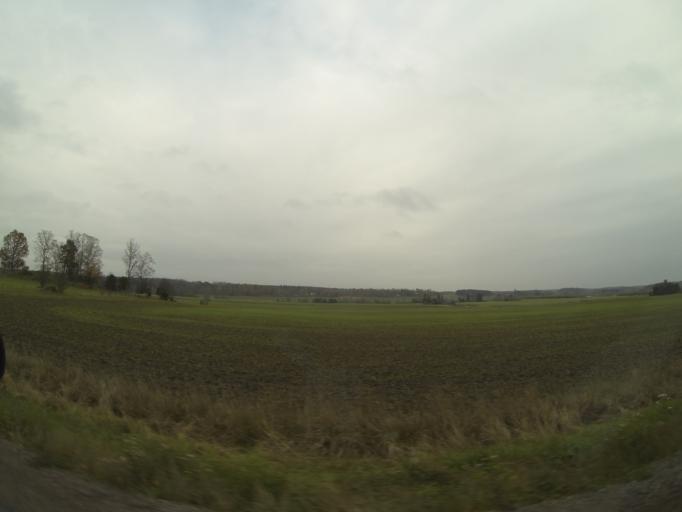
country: SE
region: Vaestmanland
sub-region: Vasteras
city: Skultuna
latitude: 59.6673
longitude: 16.4602
